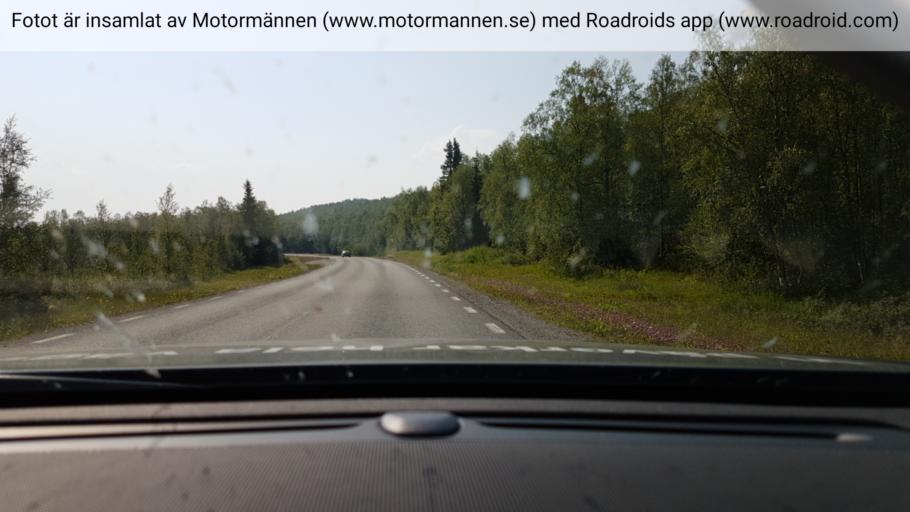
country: NO
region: Nordland
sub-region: Rana
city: Mo i Rana
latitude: 65.7723
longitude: 15.1121
